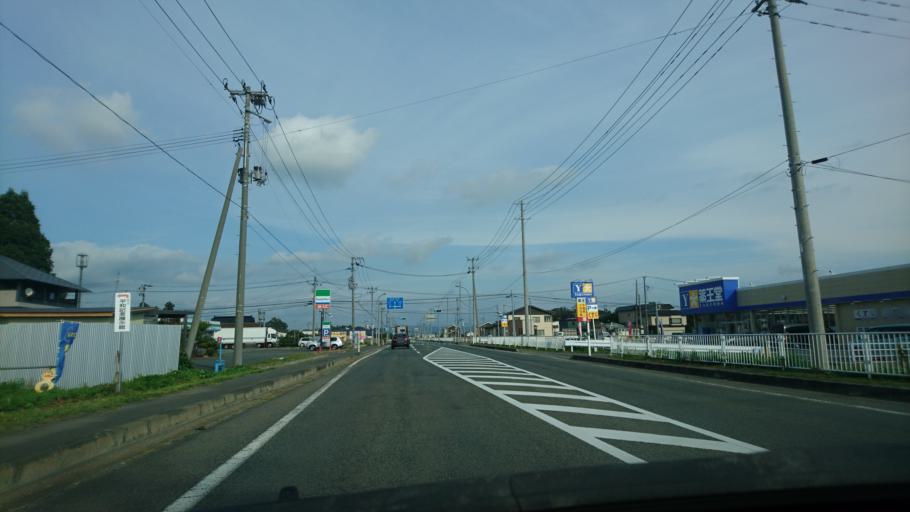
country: JP
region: Iwate
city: Kitakami
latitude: 39.3050
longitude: 141.0324
